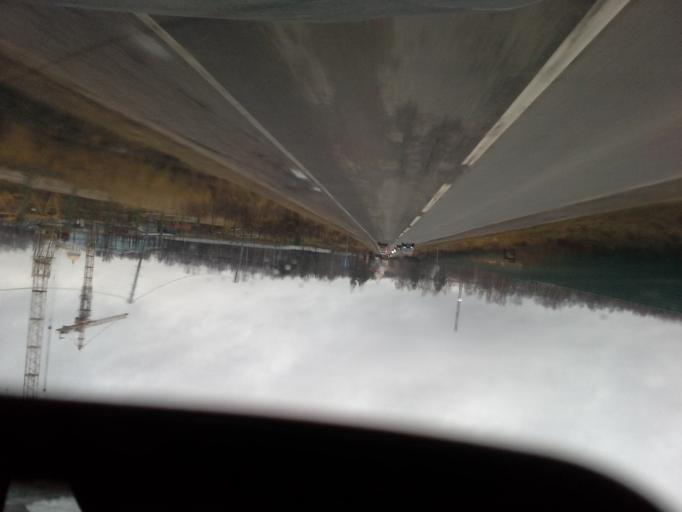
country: RU
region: Moskovskaya
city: Kokoshkino
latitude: 55.6155
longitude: 37.1605
